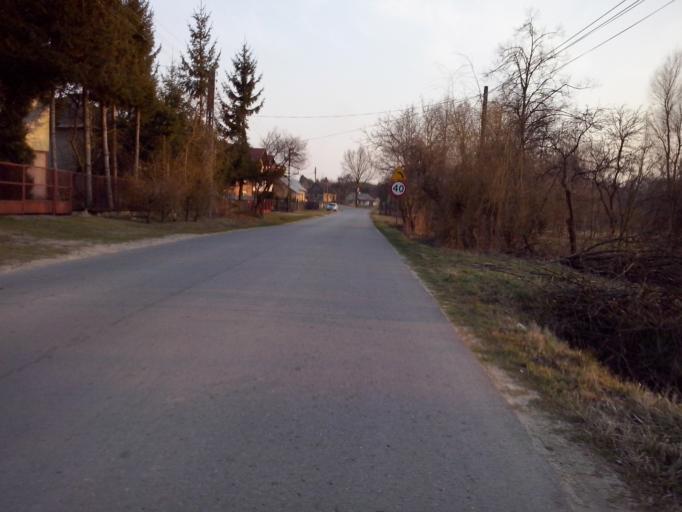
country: PL
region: Subcarpathian Voivodeship
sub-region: Powiat nizanski
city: Krzeszow
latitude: 50.3913
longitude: 22.3605
